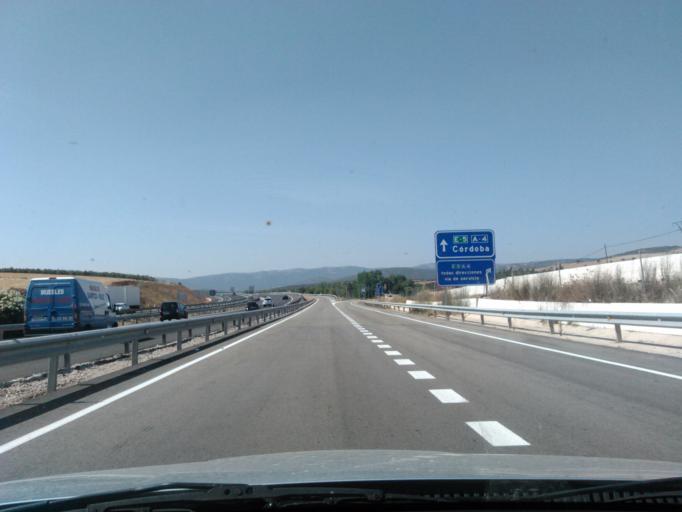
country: ES
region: Castille-La Mancha
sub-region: Provincia de Ciudad Real
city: Viso del Marques
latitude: 38.5010
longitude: -3.5018
